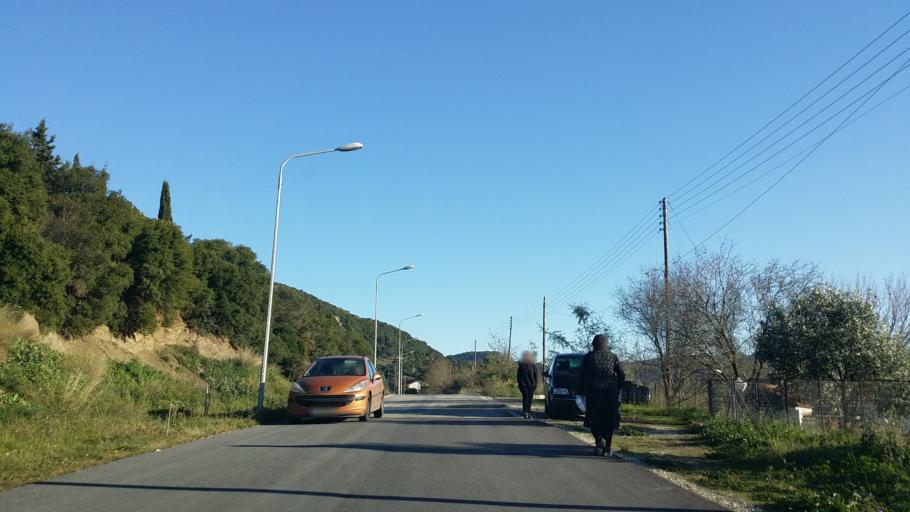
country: GR
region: West Greece
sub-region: Nomos Aitolias kai Akarnanias
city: Sardinia
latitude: 38.8743
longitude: 21.2538
